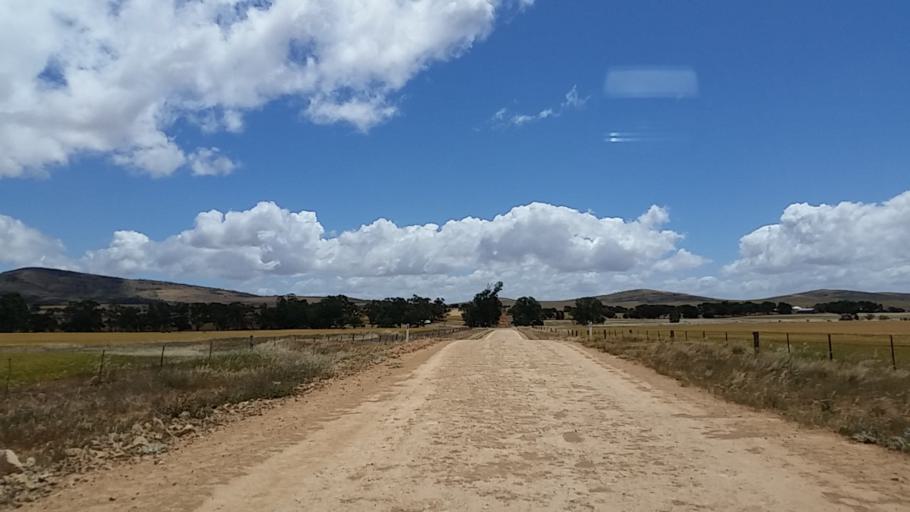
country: AU
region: South Australia
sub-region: Peterborough
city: Peterborough
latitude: -32.8502
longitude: 138.5506
